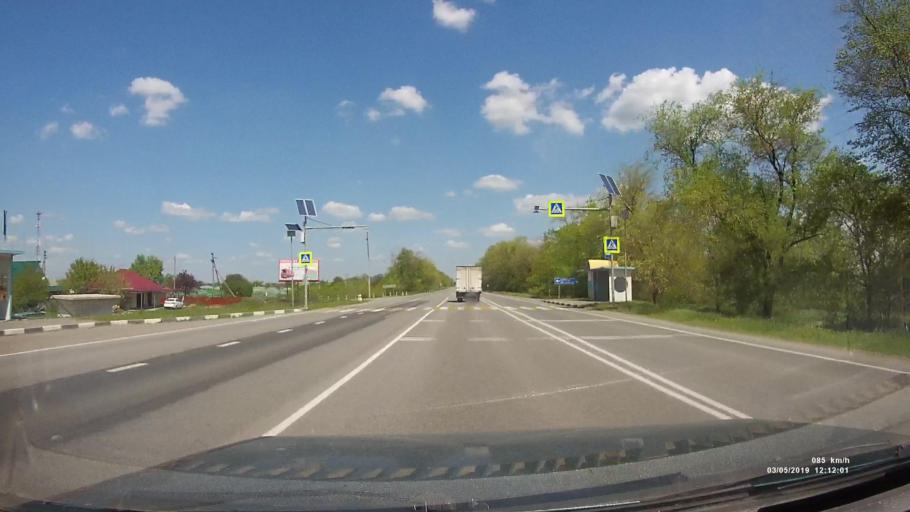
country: RU
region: Rostov
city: Bagayevskaya
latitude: 47.3168
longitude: 40.5430
